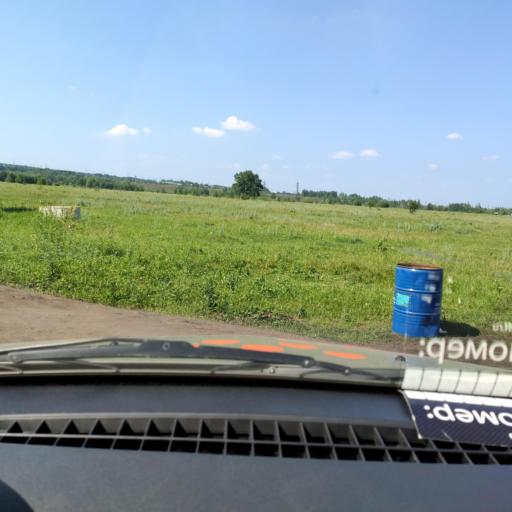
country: RU
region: Bashkortostan
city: Avdon
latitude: 54.6542
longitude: 55.8070
